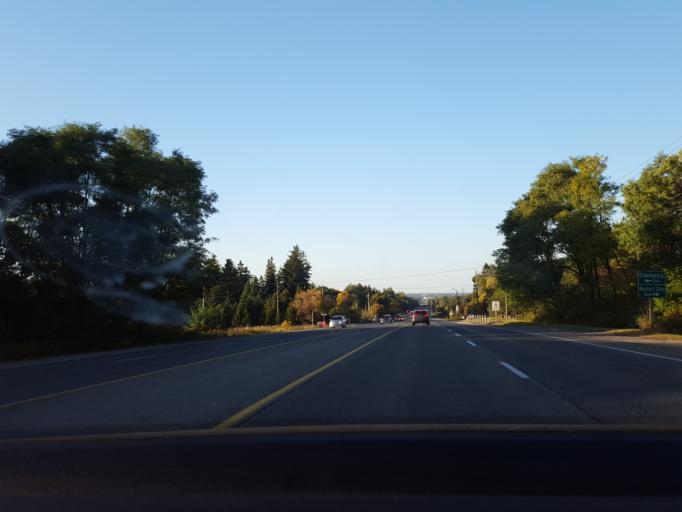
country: CA
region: Ontario
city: Newmarket
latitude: 43.9669
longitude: -79.4597
